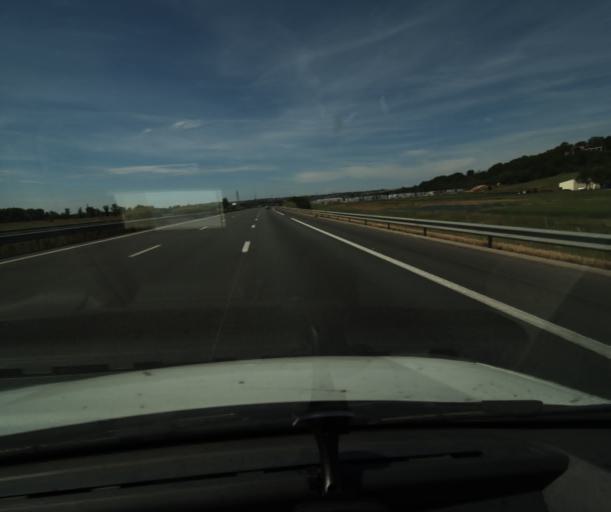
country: FR
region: Midi-Pyrenees
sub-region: Departement de la Haute-Garonne
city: Saint-Sauveur
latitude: 43.7432
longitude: 1.3900
